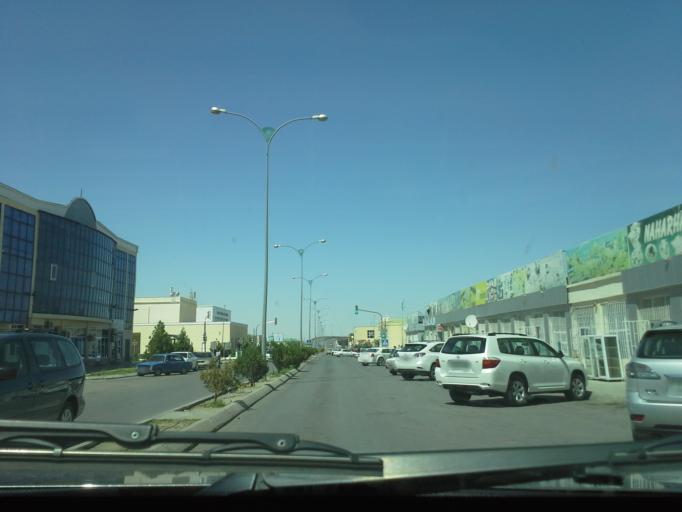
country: TM
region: Balkan
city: Serdar
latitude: 38.9734
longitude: 56.2778
